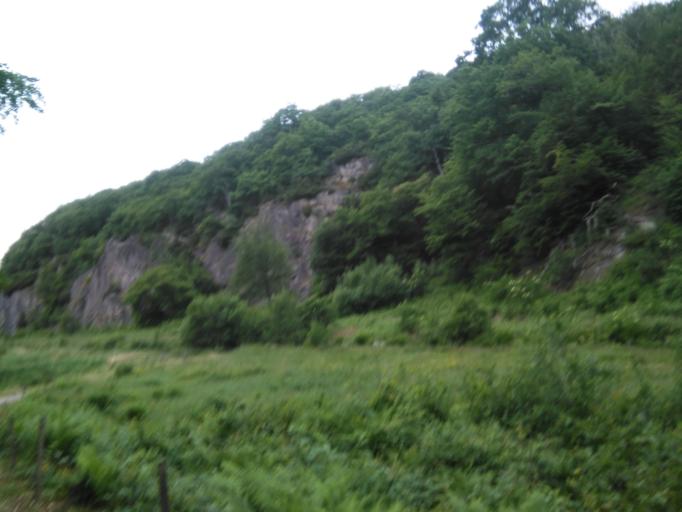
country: DK
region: Capital Region
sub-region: Bornholm Kommune
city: Akirkeby
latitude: 55.1091
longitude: 14.9017
